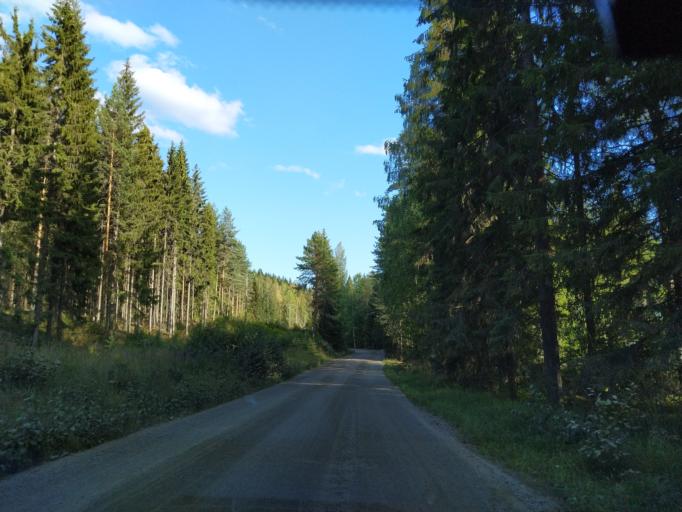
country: FI
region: Central Finland
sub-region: Jaemsae
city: Kuhmoinen
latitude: 61.7072
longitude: 24.9155
